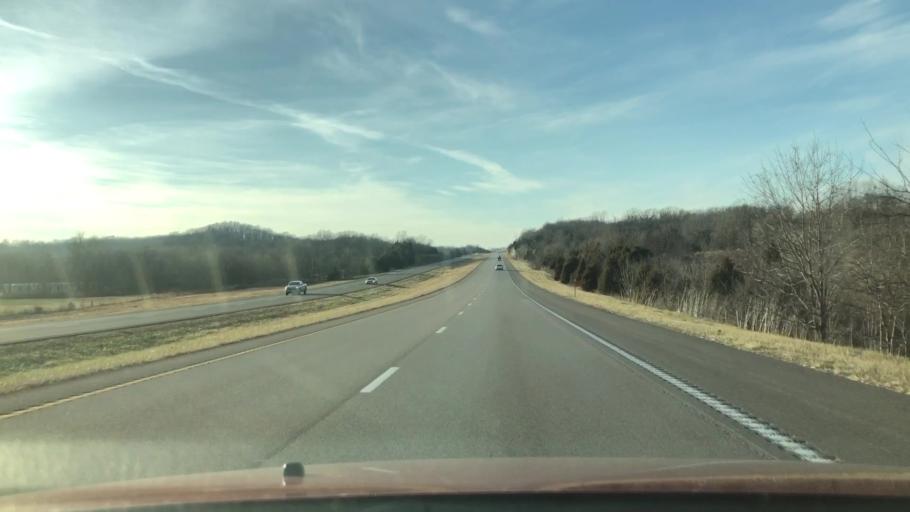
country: US
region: Missouri
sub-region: Wright County
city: Mansfield
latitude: 37.1116
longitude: -92.6538
